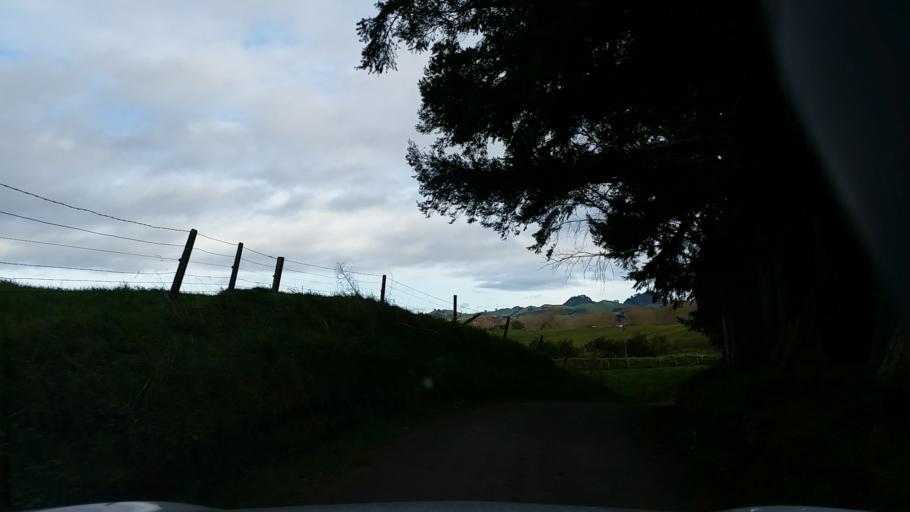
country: NZ
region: Bay of Plenty
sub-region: Rotorua District
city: Rotorua
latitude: -38.4534
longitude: 176.3403
